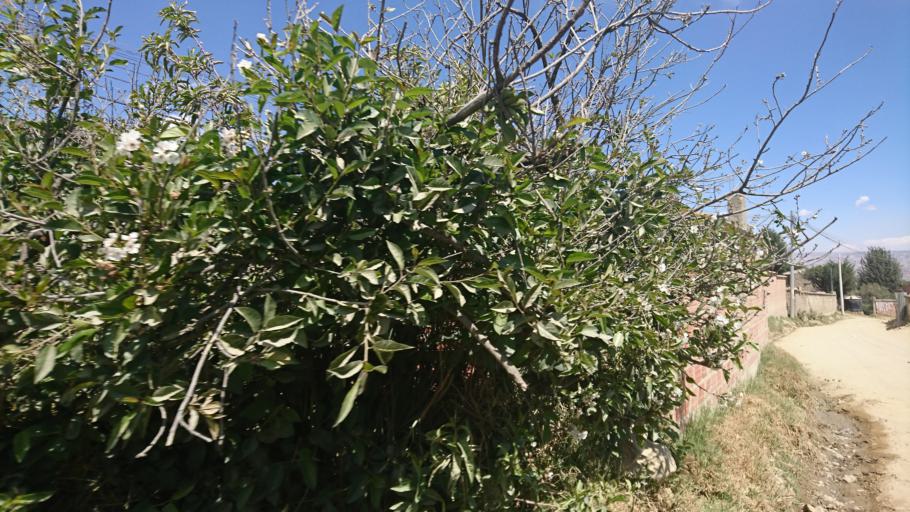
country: BO
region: La Paz
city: La Paz
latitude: -16.4894
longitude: -68.0801
